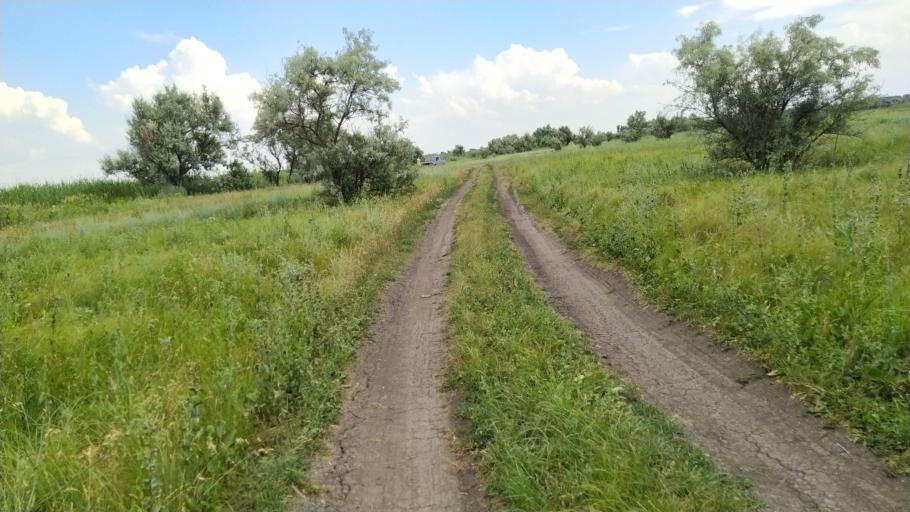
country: RU
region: Rostov
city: Kuleshovka
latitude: 47.1296
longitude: 39.6295
